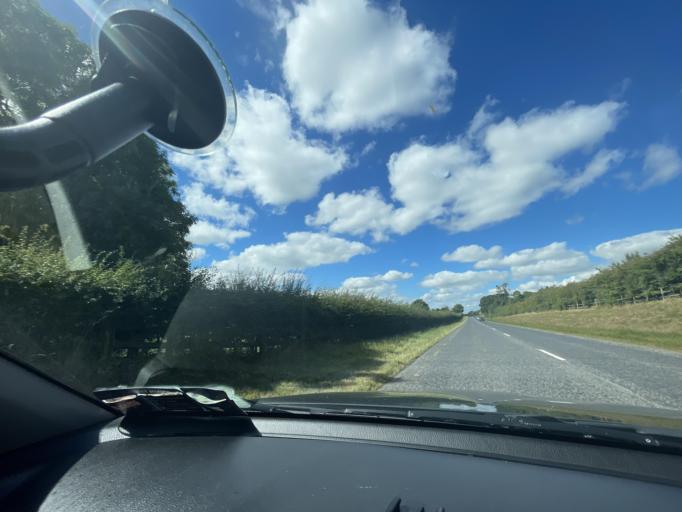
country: IE
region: Leinster
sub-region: An Mhi
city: Newtown Trim
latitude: 53.5328
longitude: -6.6984
